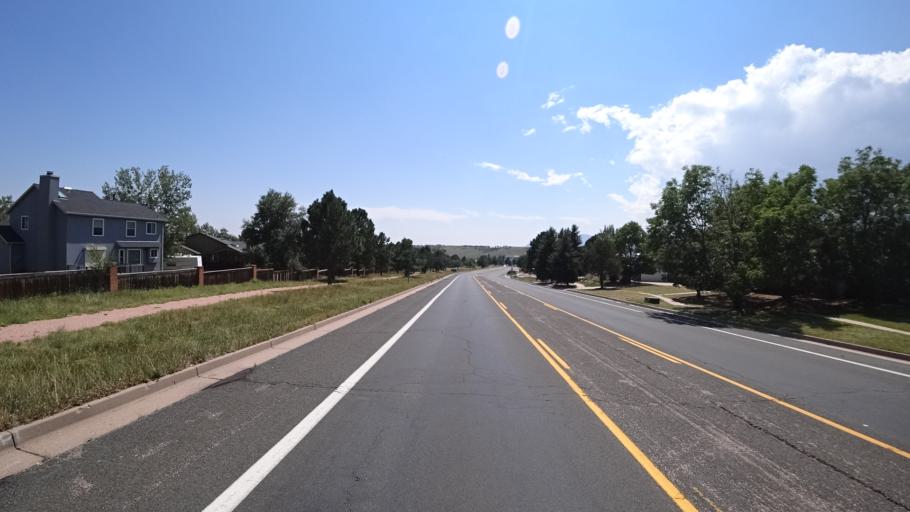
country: US
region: Colorado
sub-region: El Paso County
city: Manitou Springs
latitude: 38.9055
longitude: -104.8718
